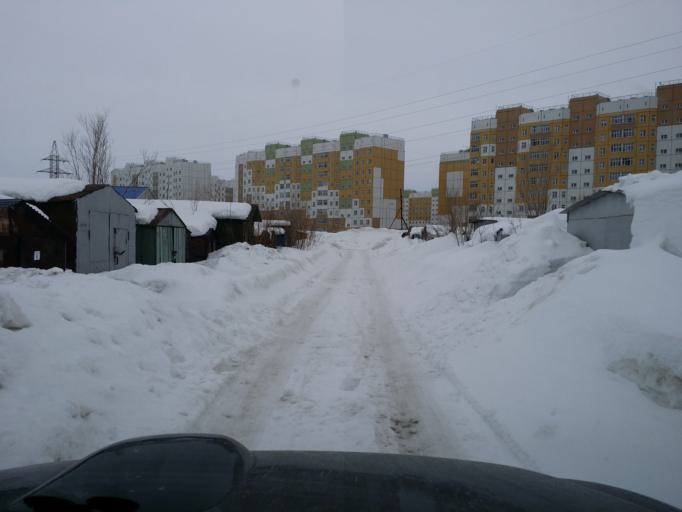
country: RU
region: Khanty-Mansiyskiy Avtonomnyy Okrug
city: Nizhnevartovsk
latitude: 60.9386
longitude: 76.6211
